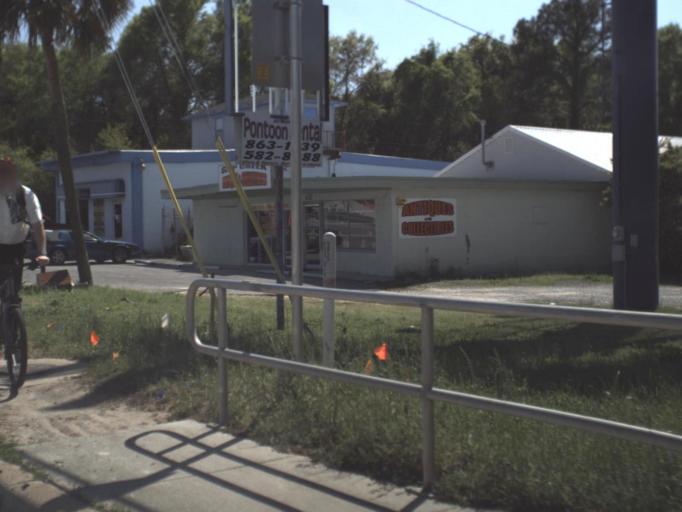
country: US
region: Florida
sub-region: Okaloosa County
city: Wright
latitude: 30.4319
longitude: -86.6397
